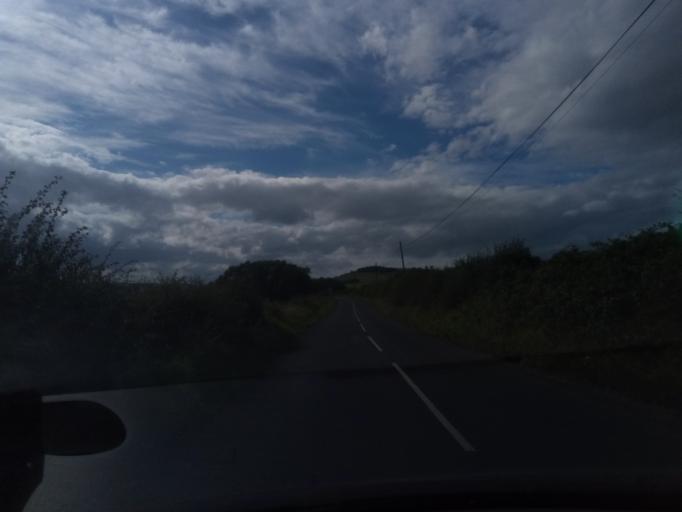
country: GB
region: Scotland
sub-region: The Scottish Borders
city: Coldstream
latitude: 55.5945
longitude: -2.1985
